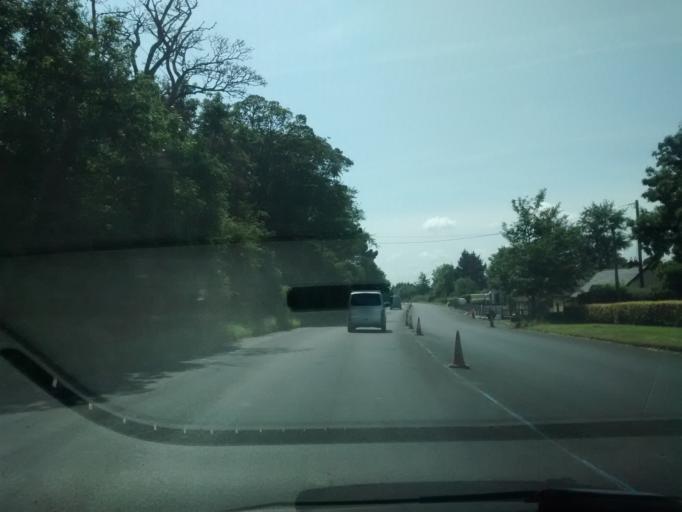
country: IE
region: Leinster
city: Lusk
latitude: 53.5112
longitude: -6.1921
